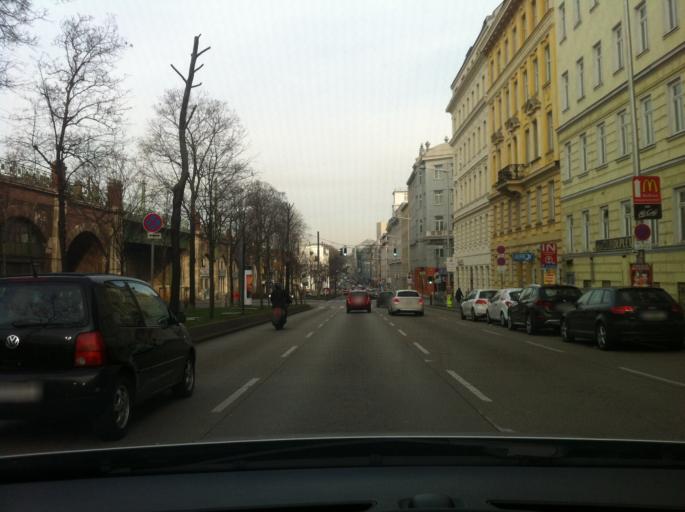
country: AT
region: Vienna
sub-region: Wien Stadt
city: Vienna
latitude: 48.2144
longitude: 16.3409
